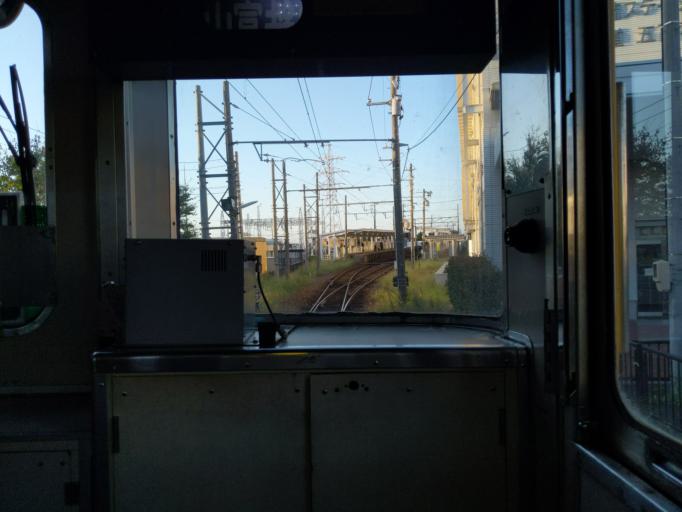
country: JP
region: Toyama
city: Kamiichi
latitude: 36.6646
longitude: 137.3146
